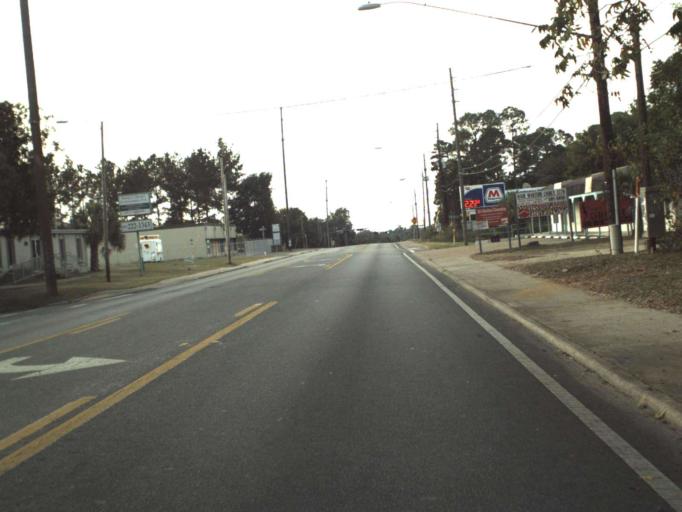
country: US
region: Florida
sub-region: Leon County
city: Tallahassee
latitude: 30.4225
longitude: -84.2821
